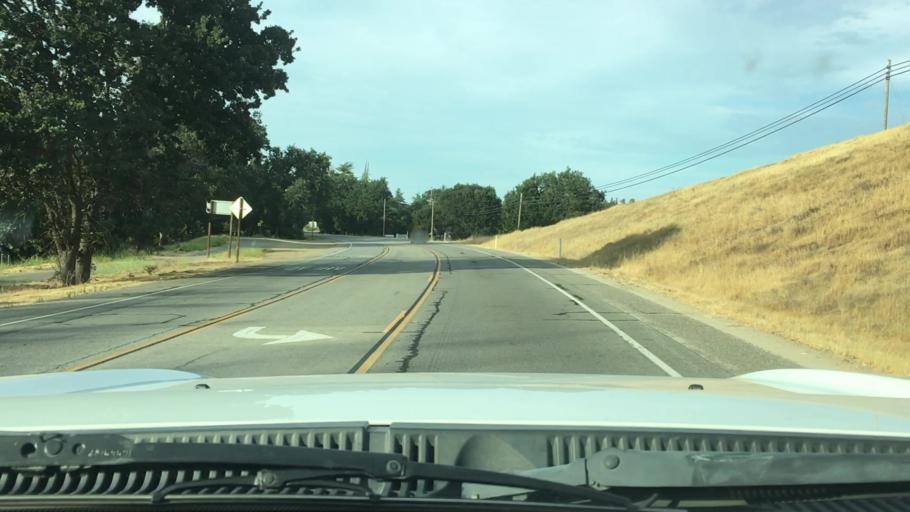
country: US
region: California
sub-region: San Luis Obispo County
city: Atascadero
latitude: 35.4634
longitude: -120.6739
